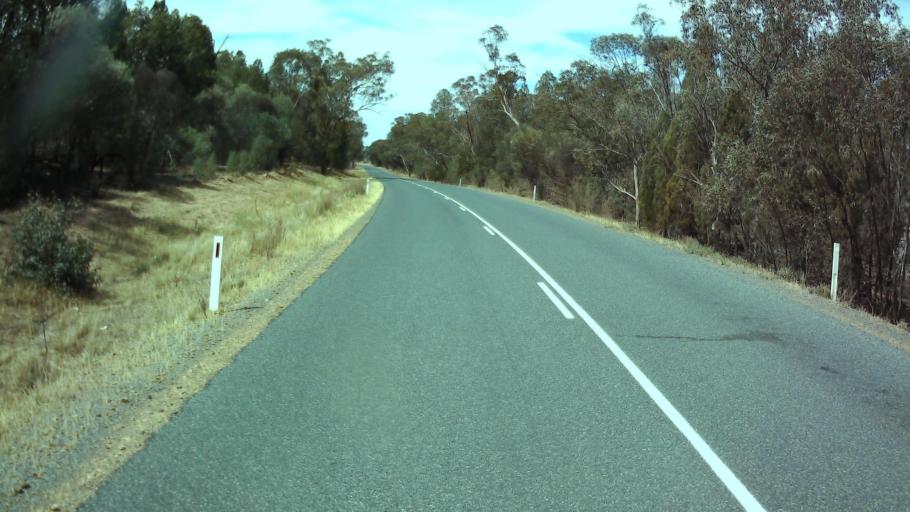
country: AU
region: New South Wales
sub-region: Weddin
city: Grenfell
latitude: -33.6699
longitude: 148.2962
